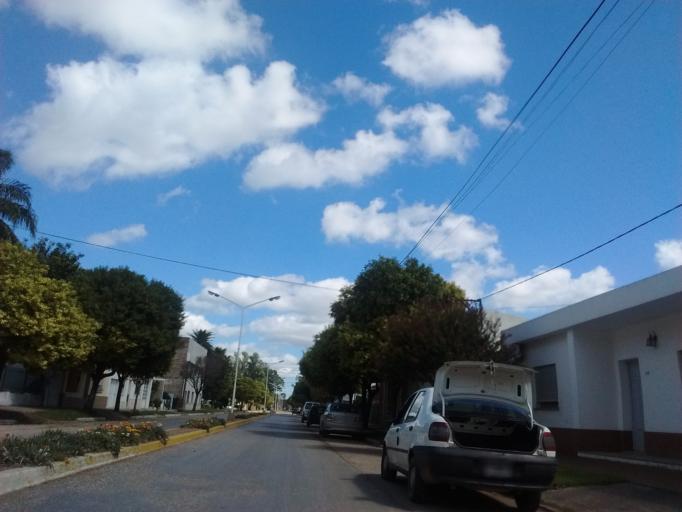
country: AR
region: Santa Fe
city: Galvez
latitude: -31.9041
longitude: -61.2765
